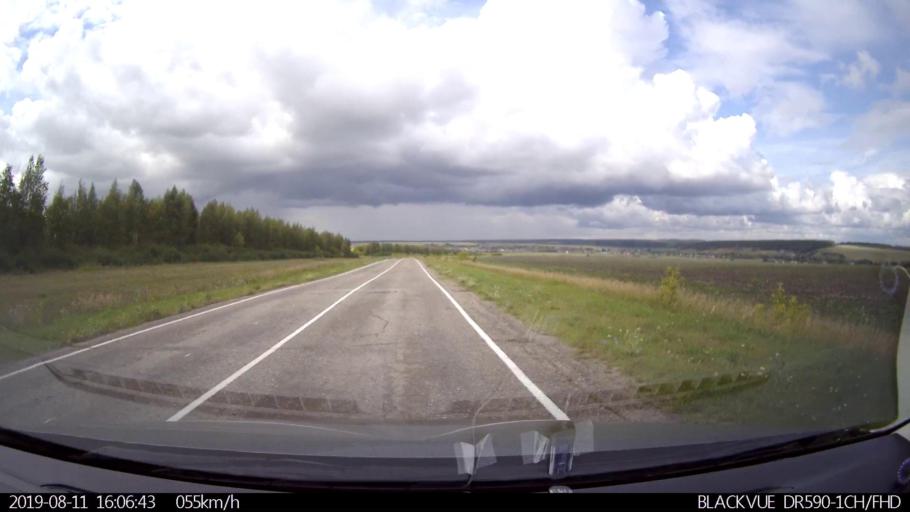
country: RU
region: Ulyanovsk
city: Ignatovka
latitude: 53.9712
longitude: 47.6477
